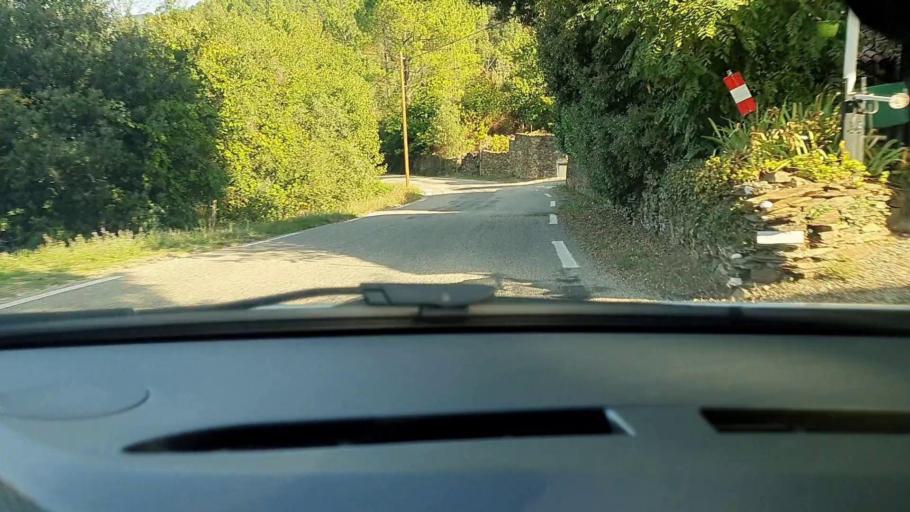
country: FR
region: Languedoc-Roussillon
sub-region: Departement du Gard
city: Besseges
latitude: 44.3077
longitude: 4.0582
